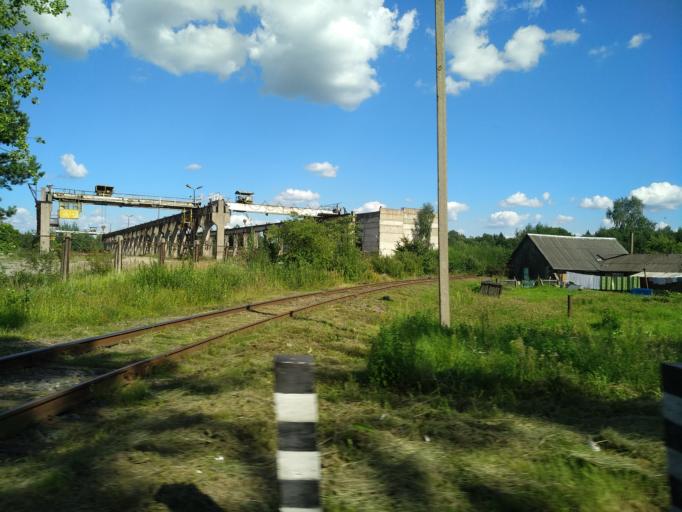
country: BY
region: Vitebsk
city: Mosar
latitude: 55.1235
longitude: 27.2109
